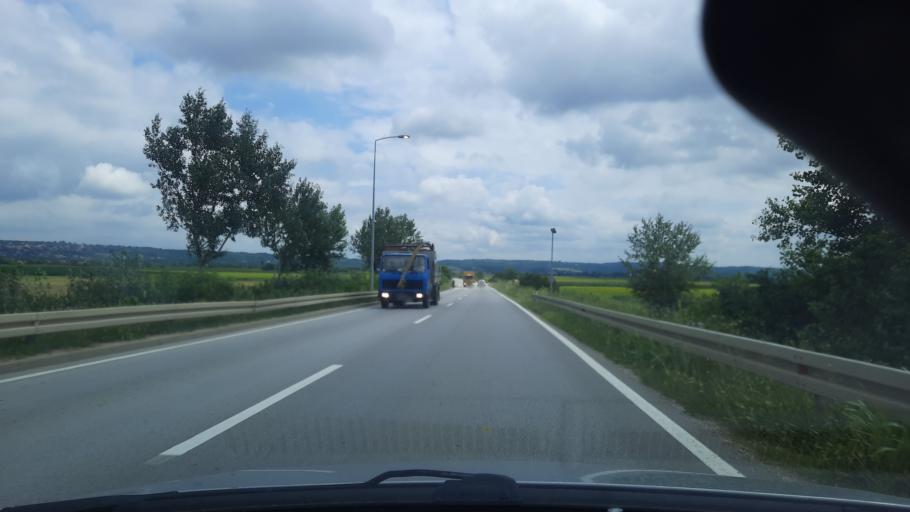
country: RS
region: Central Serbia
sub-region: Branicevski Okrug
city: Pozarevac
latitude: 44.5962
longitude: 21.1579
